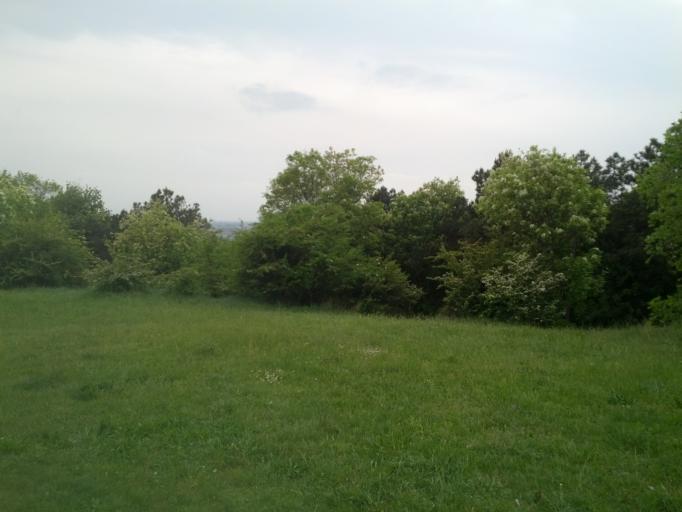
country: IT
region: Veneto
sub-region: Provincia di Verona
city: Montorio
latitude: 45.4665
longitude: 11.0511
